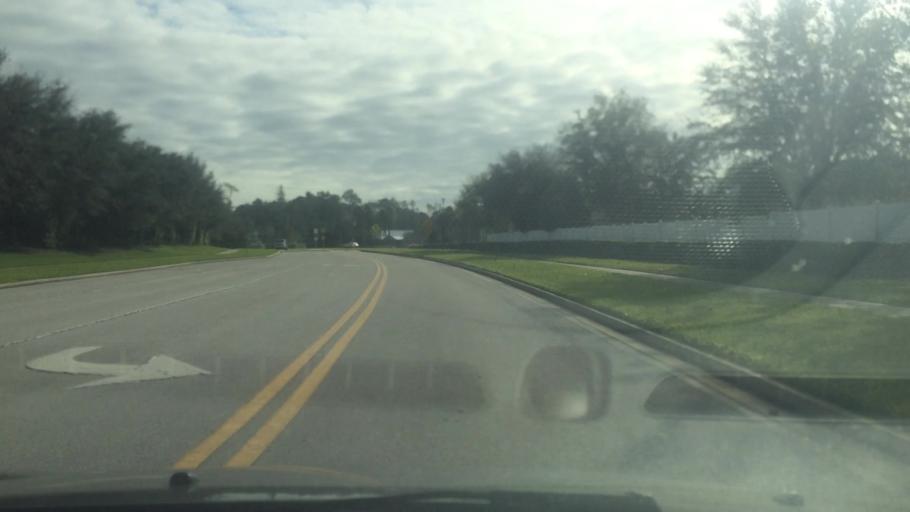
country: US
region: Florida
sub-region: Saint Johns County
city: Saint Augustine
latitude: 29.9277
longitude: -81.3614
